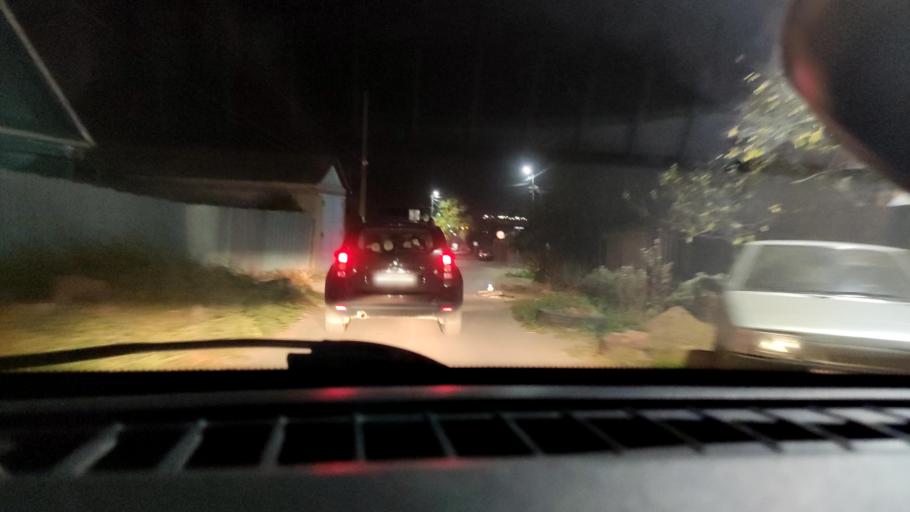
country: RU
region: Samara
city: Samara
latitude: 53.1817
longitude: 50.1879
